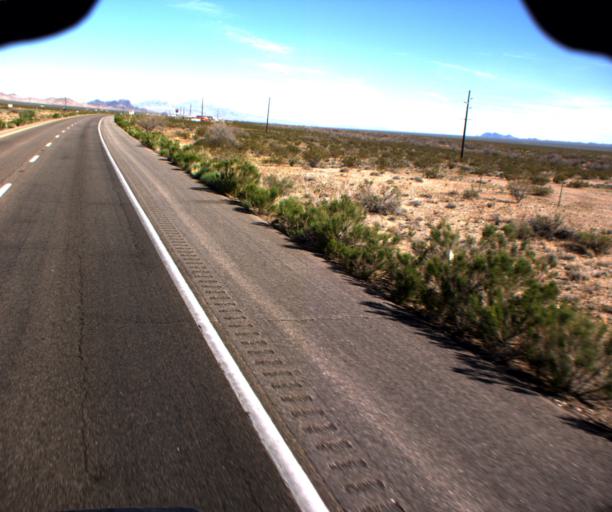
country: US
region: Arizona
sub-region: Mohave County
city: Dolan Springs
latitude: 35.6779
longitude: -114.4644
